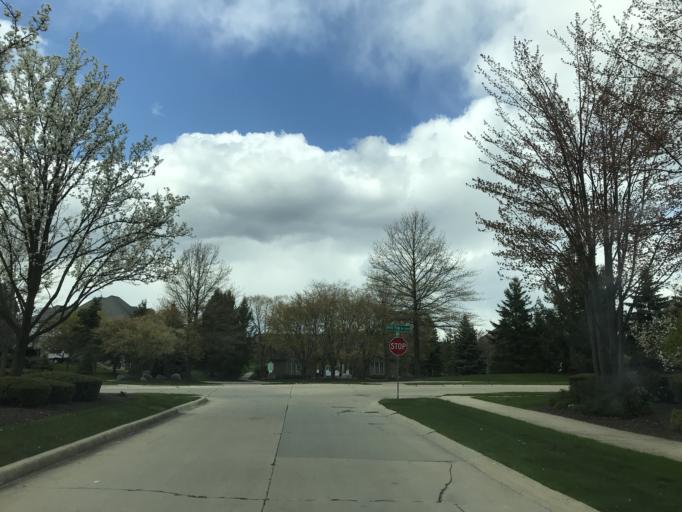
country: US
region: Michigan
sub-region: Wayne County
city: Plymouth
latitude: 42.3773
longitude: -83.5165
